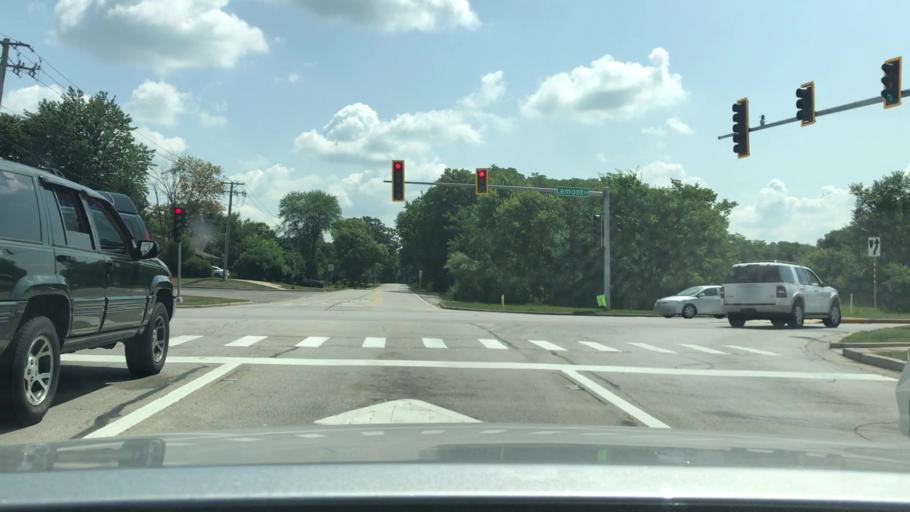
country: US
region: Illinois
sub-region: DuPage County
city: Woodridge
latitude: 41.7292
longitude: -88.0121
